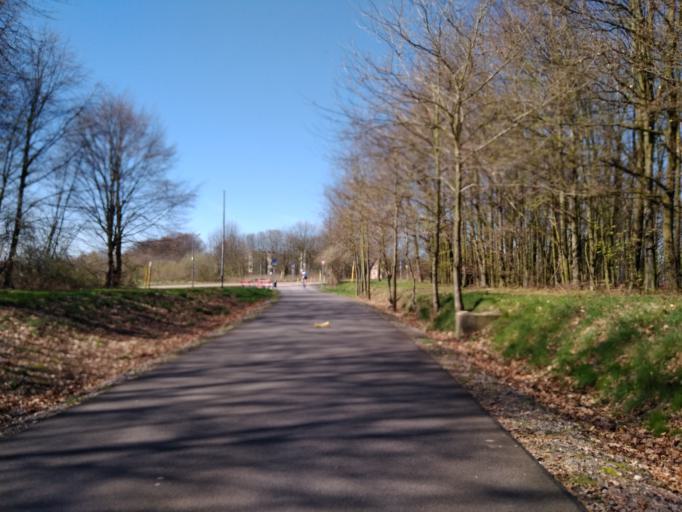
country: DE
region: North Rhine-Westphalia
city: Herten
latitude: 51.6100
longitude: 7.1344
